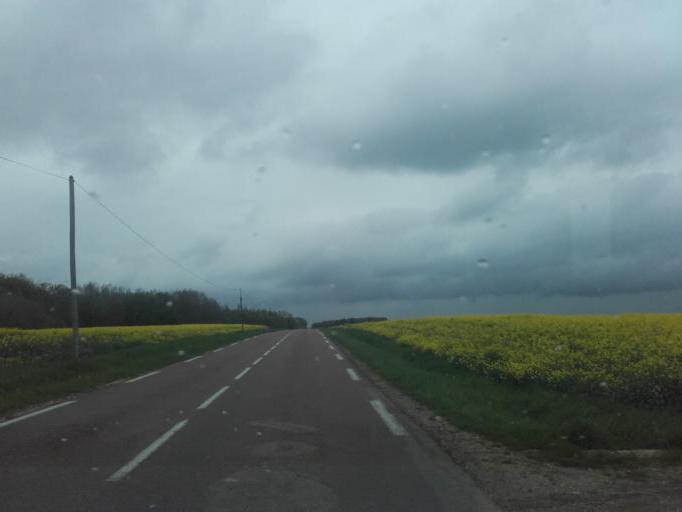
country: FR
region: Bourgogne
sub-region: Departement de l'Yonne
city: Joux-la-Ville
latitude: 47.6933
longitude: 3.8641
